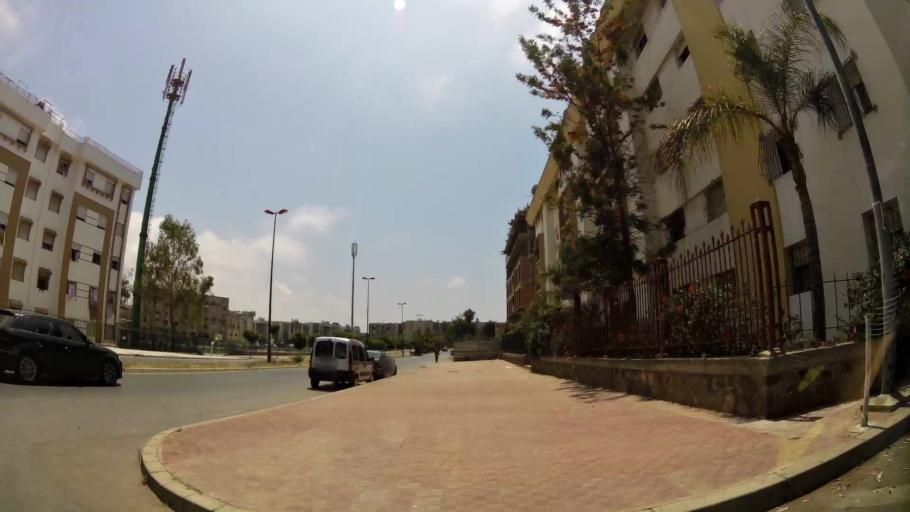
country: MA
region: Rabat-Sale-Zemmour-Zaer
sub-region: Skhirate-Temara
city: Temara
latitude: 33.9711
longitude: -6.8975
